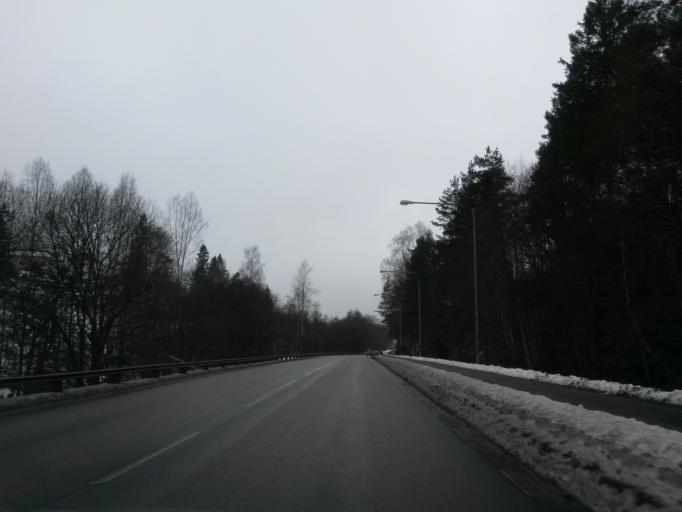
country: SE
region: Vaestra Goetaland
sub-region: Boras Kommun
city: Boras
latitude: 57.7051
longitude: 12.9628
